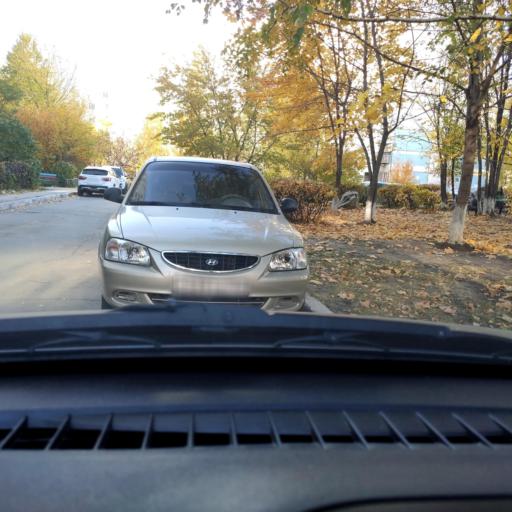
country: RU
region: Samara
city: Tol'yatti
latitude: 53.5473
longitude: 49.3383
